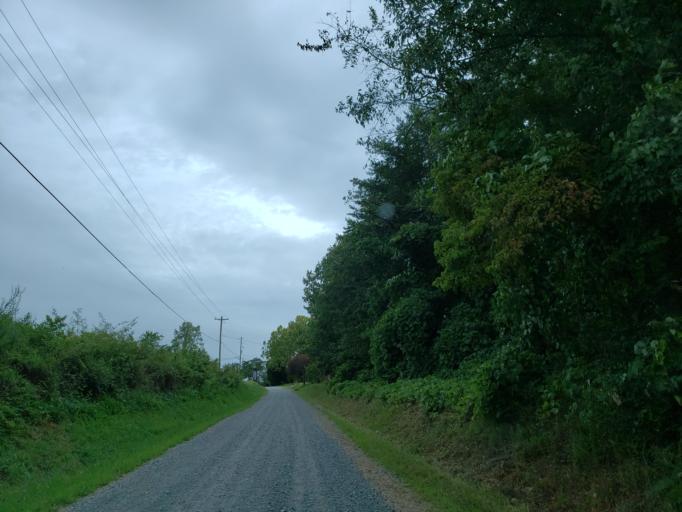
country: US
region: Georgia
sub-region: Pickens County
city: Jasper
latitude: 34.4683
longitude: -84.5181
